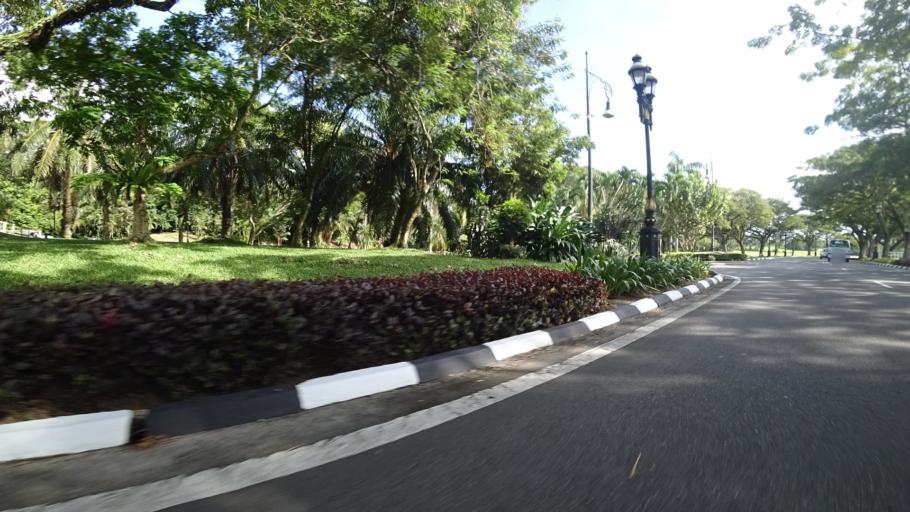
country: BN
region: Brunei and Muara
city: Bandar Seri Begawan
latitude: 4.9454
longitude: 114.8332
